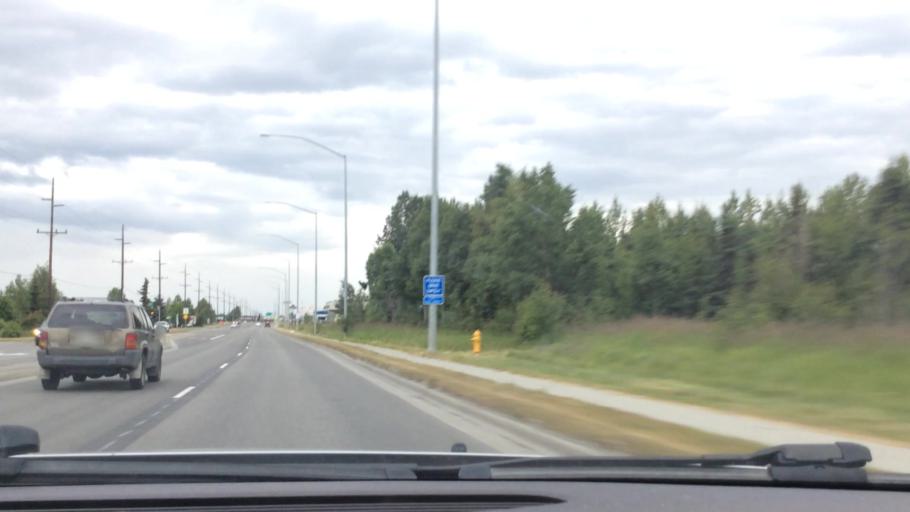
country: US
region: Alaska
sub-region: Anchorage Municipality
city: Anchorage
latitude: 61.1665
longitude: -149.8408
